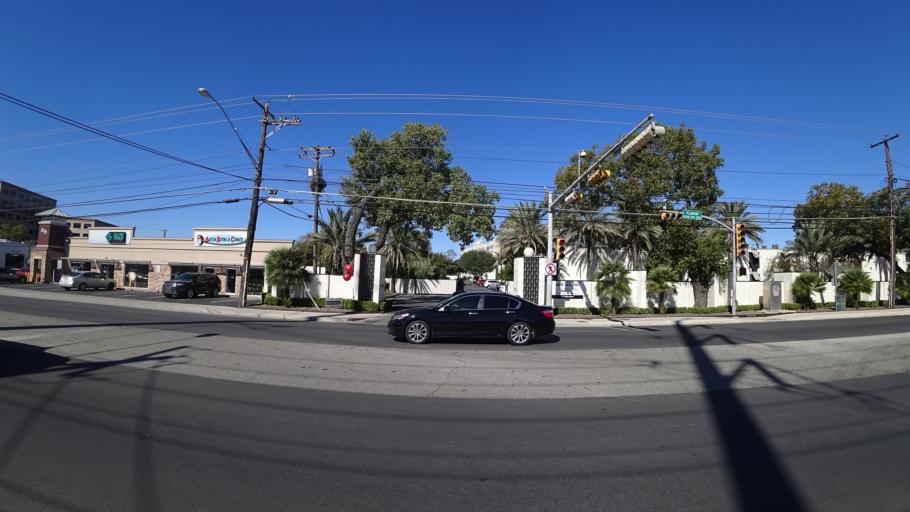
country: US
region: Texas
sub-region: Travis County
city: Austin
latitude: 30.3187
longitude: -97.7308
